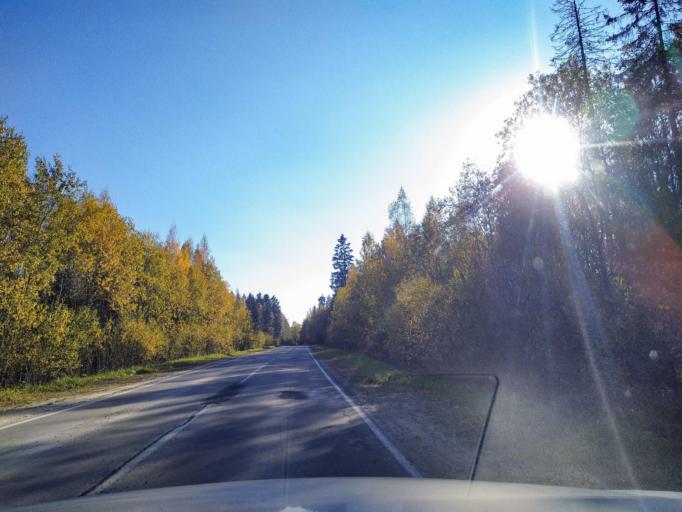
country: RU
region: Leningrad
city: Siverskiy
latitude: 59.3017
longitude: 30.0356
